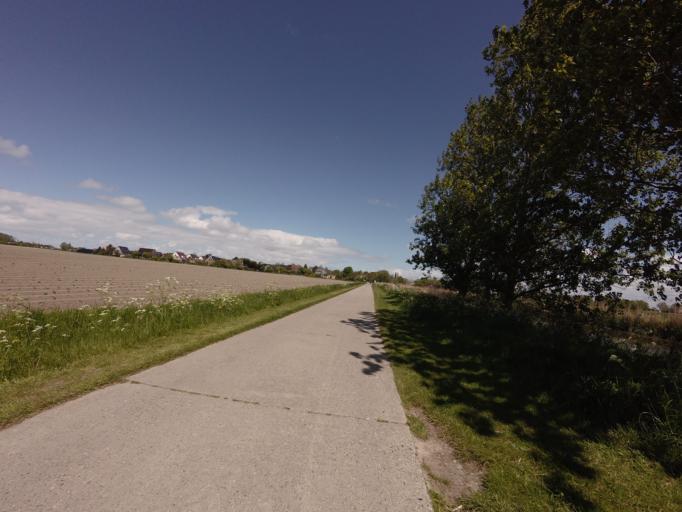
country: NL
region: Friesland
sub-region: Gemeente Harlingen
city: Harlingen
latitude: 53.1372
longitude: 5.4349
